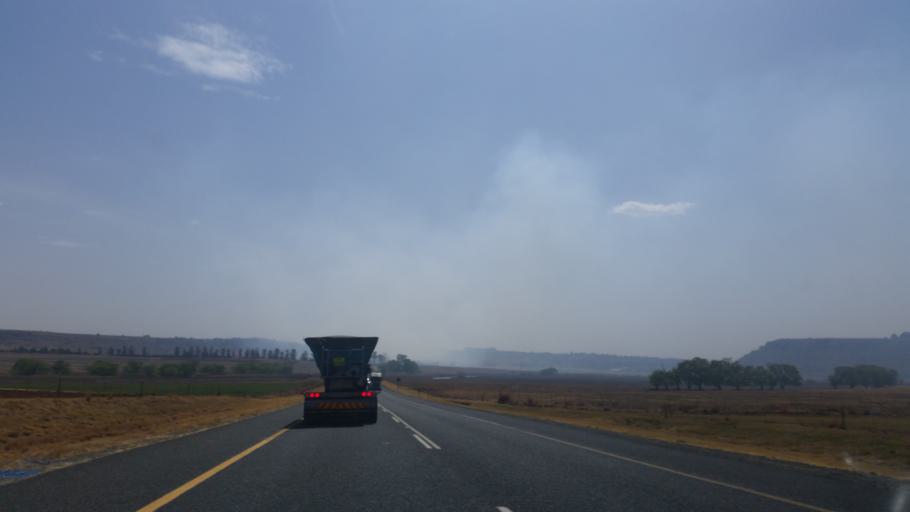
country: ZA
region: Orange Free State
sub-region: Thabo Mofutsanyana District Municipality
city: Bethlehem
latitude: -28.2748
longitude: 28.3778
